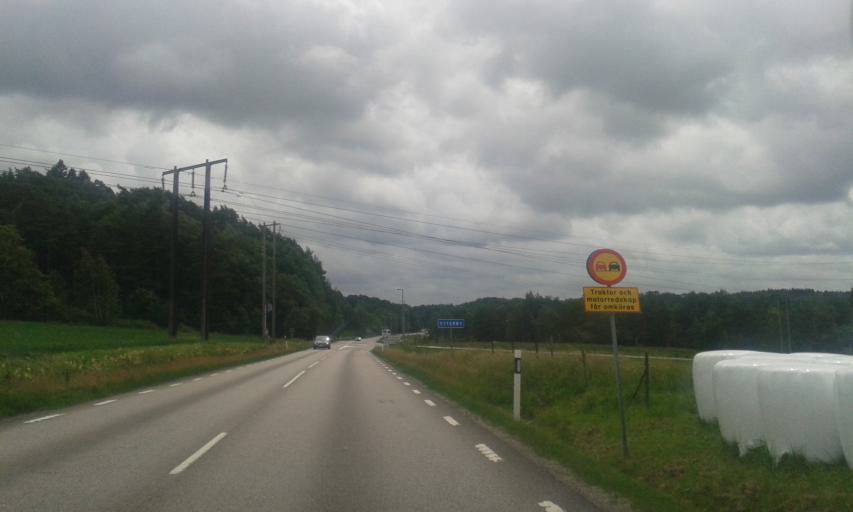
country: SE
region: Vaestra Goetaland
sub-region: Kungalvs Kommun
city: Kungalv
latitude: 57.8728
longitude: 11.9075
